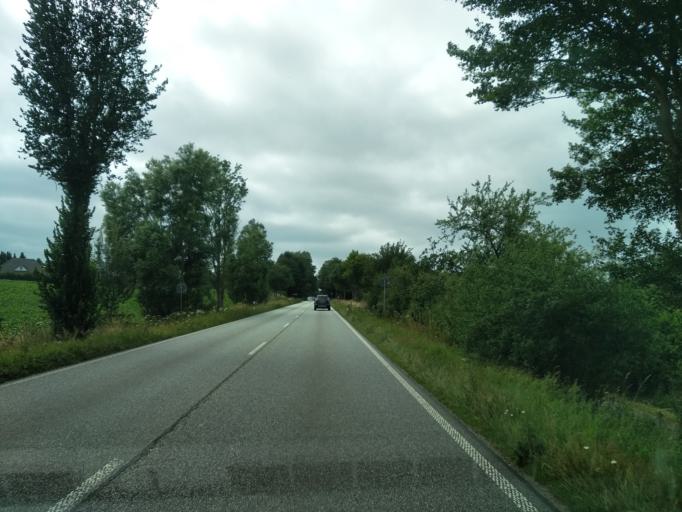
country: DE
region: Schleswig-Holstein
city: Wees
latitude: 54.8045
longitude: 9.5161
